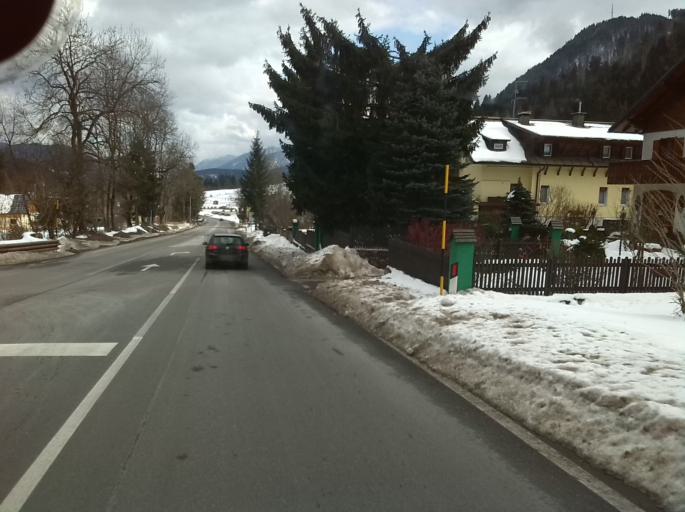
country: IT
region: Friuli Venezia Giulia
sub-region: Provincia di Udine
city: Tarvisio
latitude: 46.5072
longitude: 13.5476
